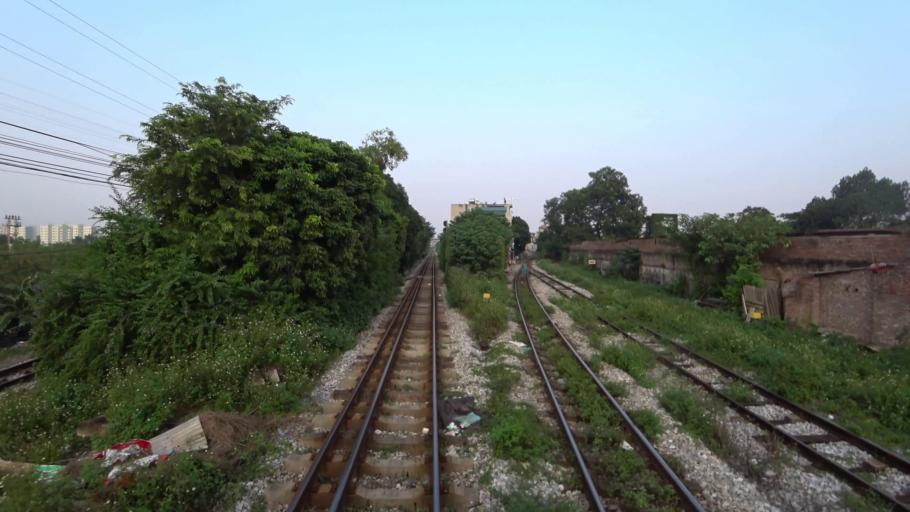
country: VN
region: Ha Noi
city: Trau Quy
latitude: 21.0692
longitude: 105.9004
